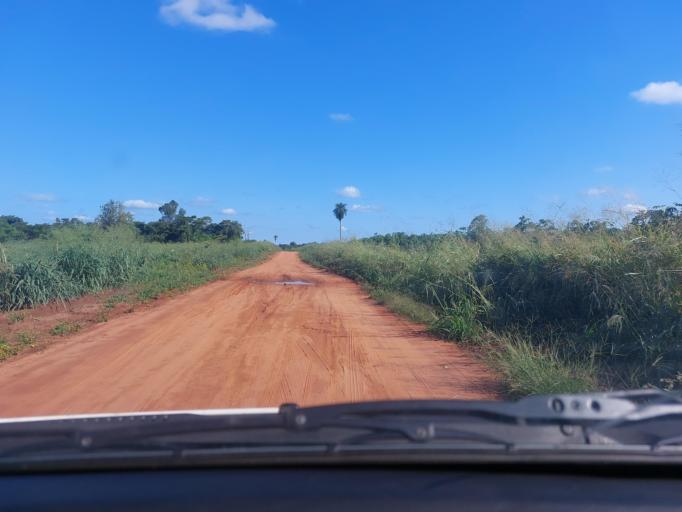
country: PY
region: San Pedro
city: Guayaybi
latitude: -24.5192
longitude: -56.5463
